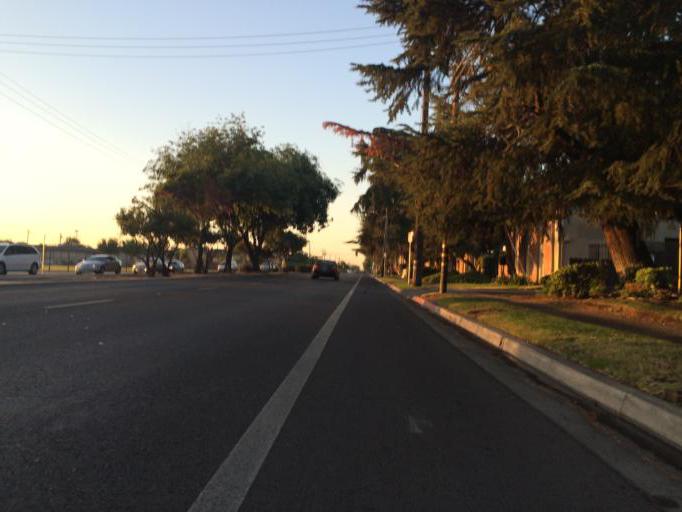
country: US
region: California
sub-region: Fresno County
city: Fresno
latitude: 36.7849
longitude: -119.7544
